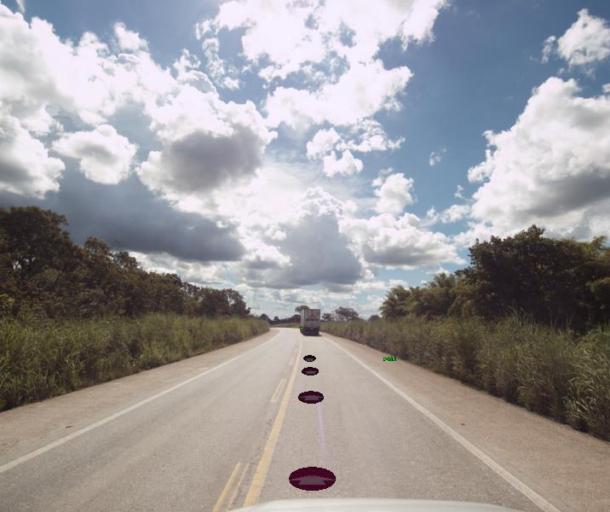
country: BR
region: Goias
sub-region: Porangatu
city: Porangatu
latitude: -13.5582
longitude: -49.0613
